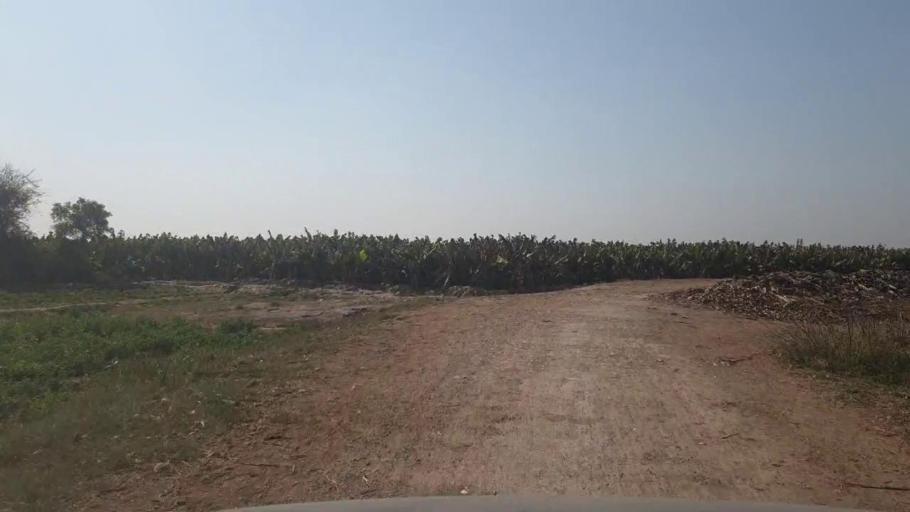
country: PK
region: Sindh
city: Chambar
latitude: 25.3583
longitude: 68.7779
